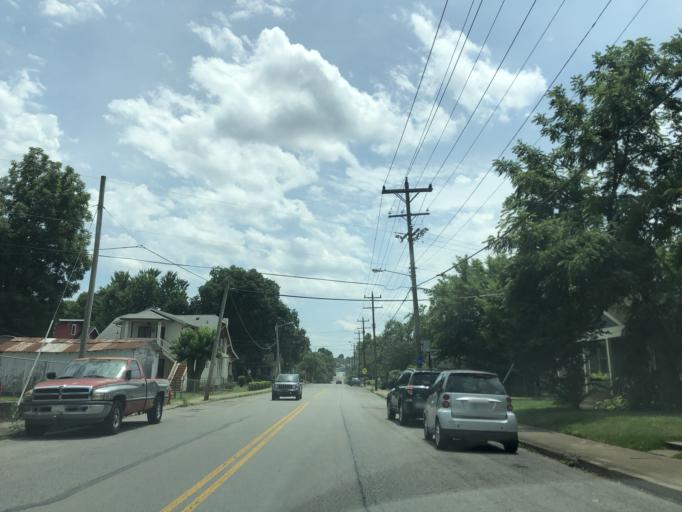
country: US
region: Tennessee
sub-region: Davidson County
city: Nashville
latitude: 36.1827
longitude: -86.7547
